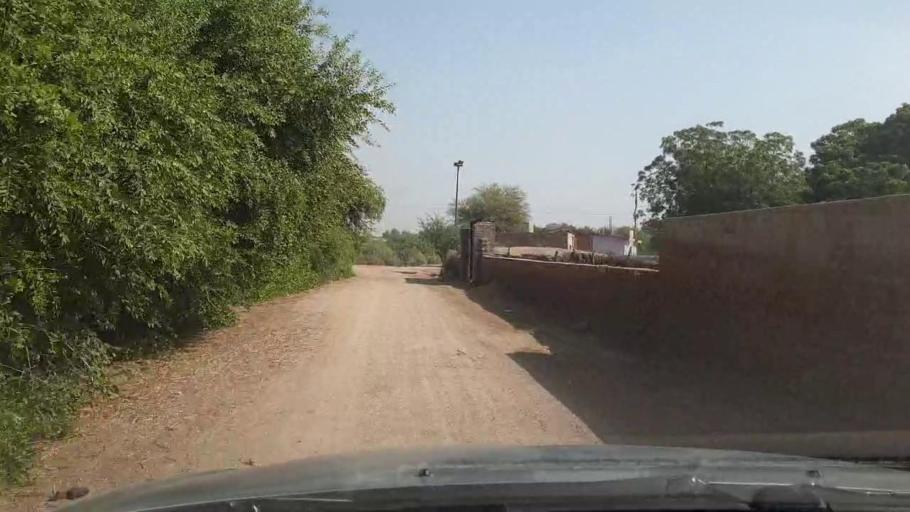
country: PK
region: Sindh
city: Tando Jam
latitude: 25.2813
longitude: 68.5343
